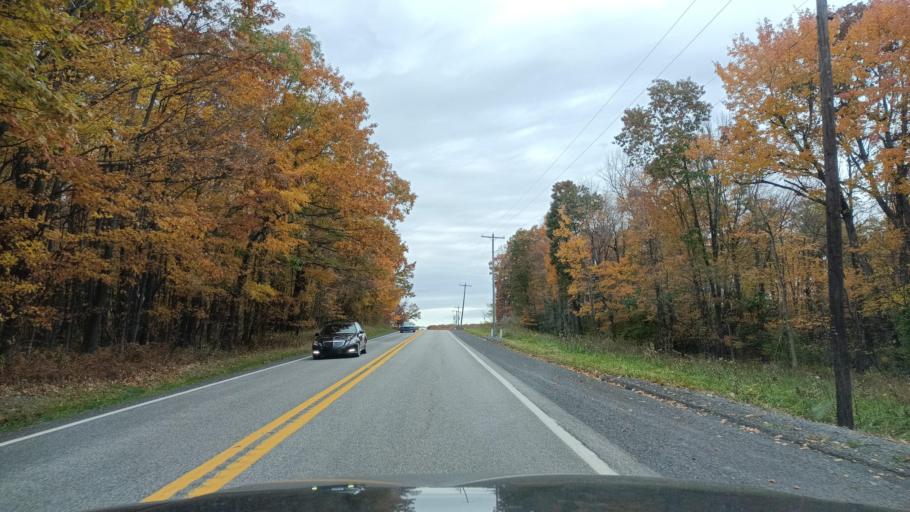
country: US
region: Maryland
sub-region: Garrett County
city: Mountain Lake Park
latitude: 39.2364
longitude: -79.2199
